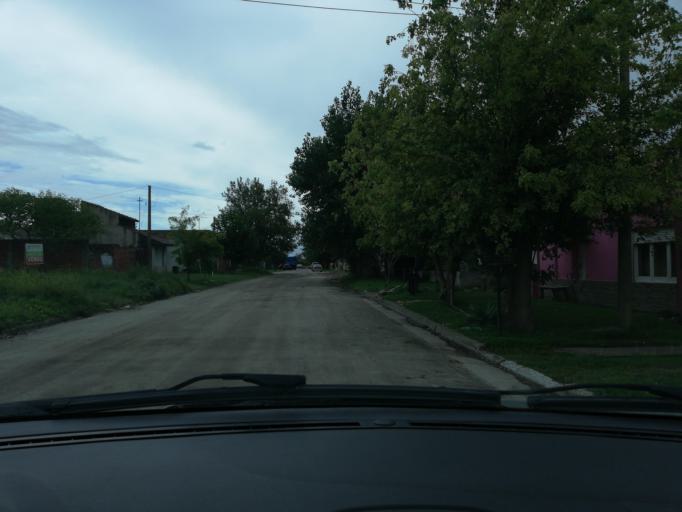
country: AR
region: Buenos Aires
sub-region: Partido de Balcarce
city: Balcarce
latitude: -37.8513
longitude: -58.2432
